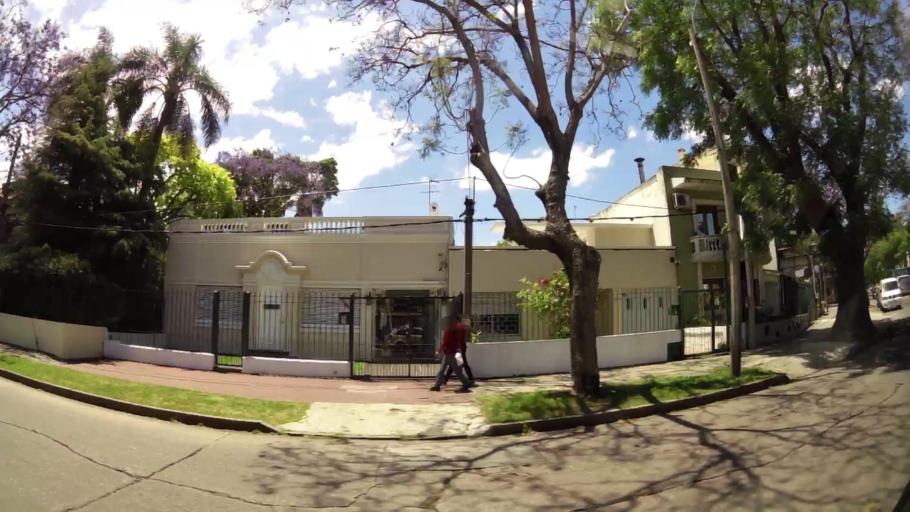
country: UY
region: Montevideo
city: Montevideo
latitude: -34.8664
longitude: -56.1966
